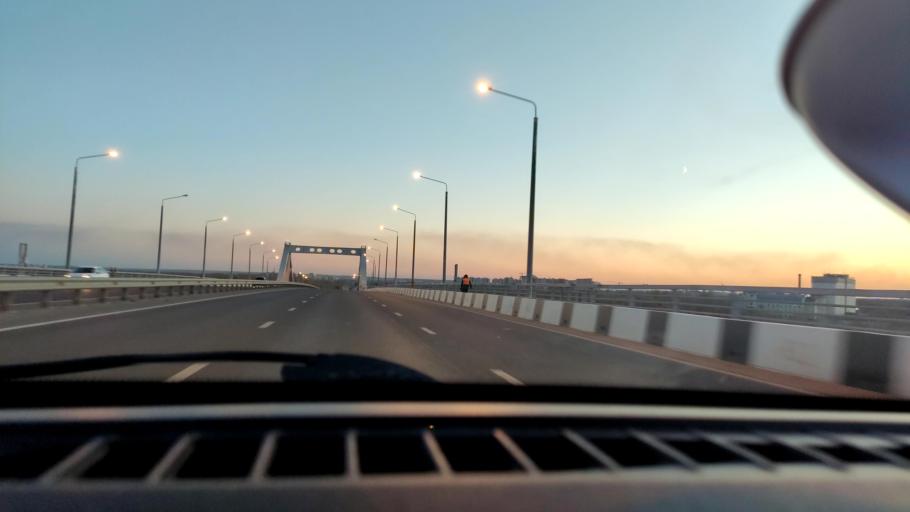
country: RU
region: Samara
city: Rozhdestveno
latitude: 53.1765
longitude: 50.0853
